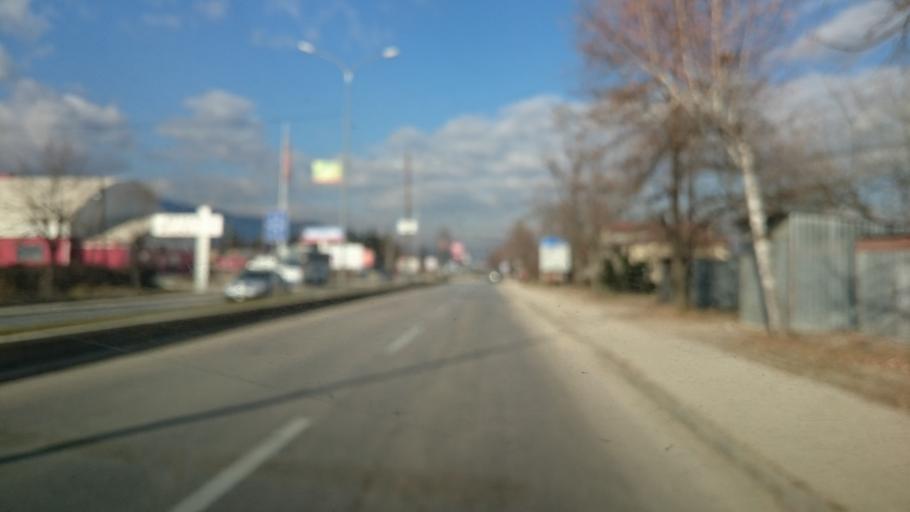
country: MK
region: Kicevo
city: Kicevo
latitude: 41.5114
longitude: 20.9524
